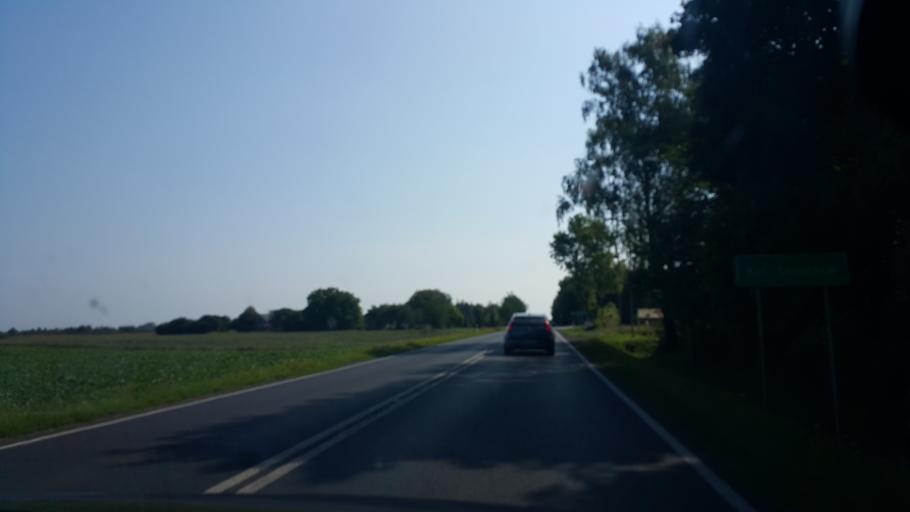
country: PL
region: Lublin Voivodeship
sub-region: Powiat leczynski
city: Spiczyn
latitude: 51.2972
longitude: 22.7834
